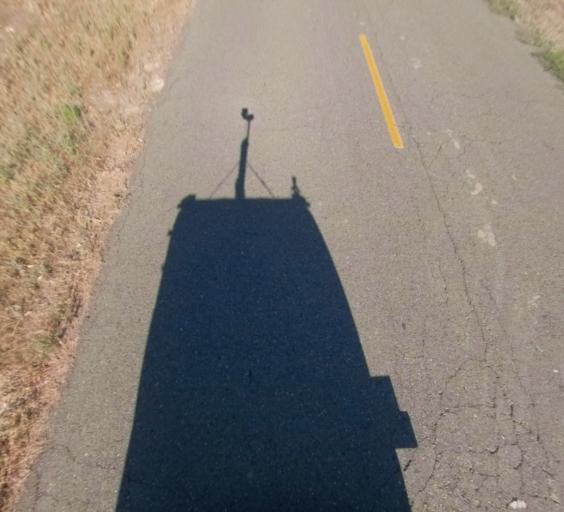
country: US
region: California
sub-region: Madera County
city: Bonadelle Ranchos-Madera Ranchos
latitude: 36.9753
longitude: -119.8821
